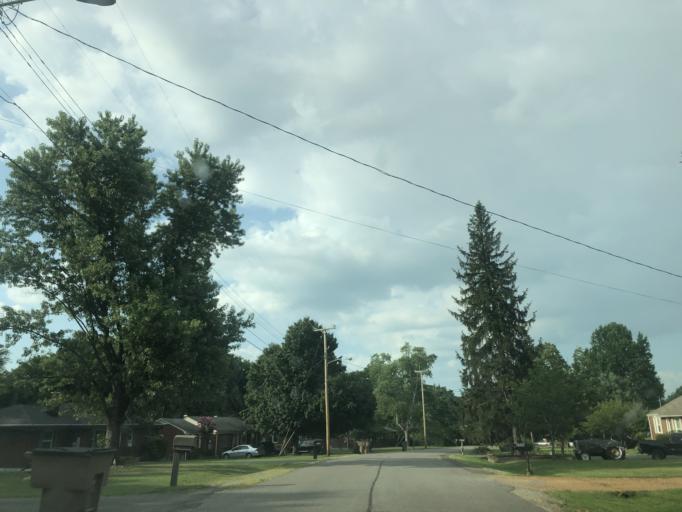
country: US
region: Tennessee
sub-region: Davidson County
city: Lakewood
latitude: 36.1585
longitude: -86.6778
